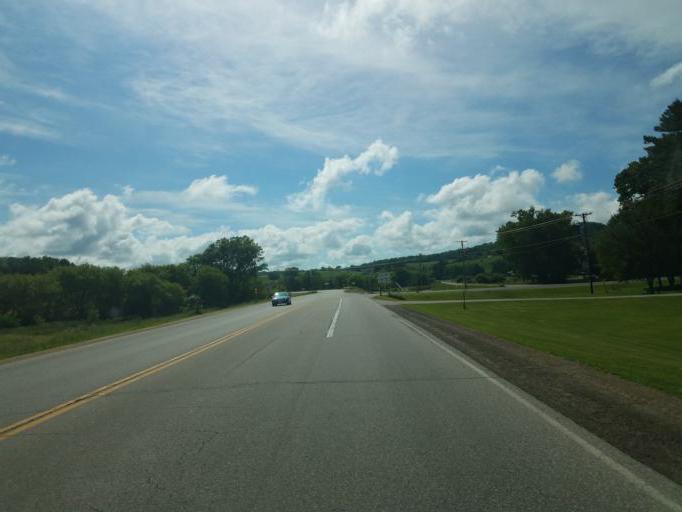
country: US
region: Wisconsin
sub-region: Monroe County
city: Tomah
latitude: 43.8328
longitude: -90.4729
